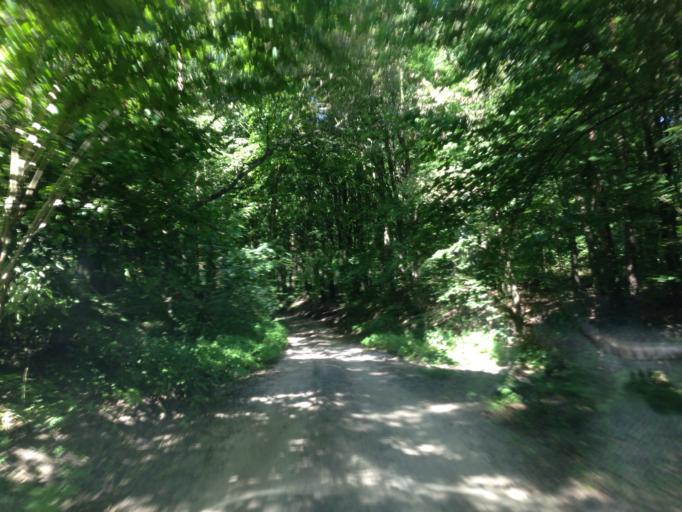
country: PL
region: Kujawsko-Pomorskie
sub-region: Powiat brodnicki
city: Gorzno
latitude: 53.2211
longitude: 19.6515
